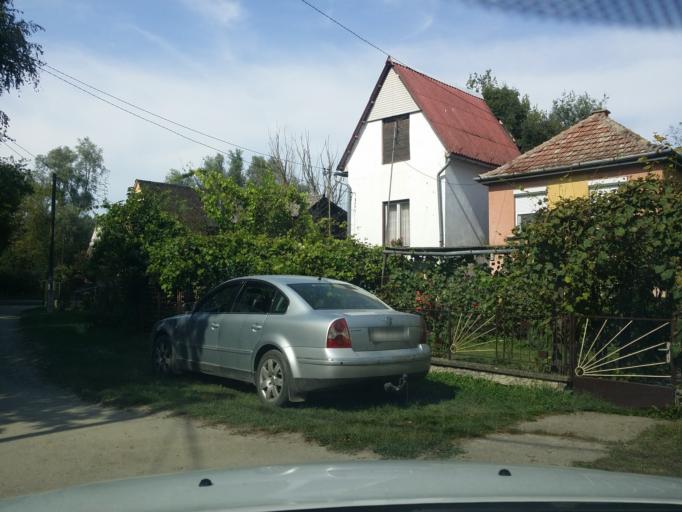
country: HU
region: Bacs-Kiskun
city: Baja
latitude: 46.1966
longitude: 18.9193
